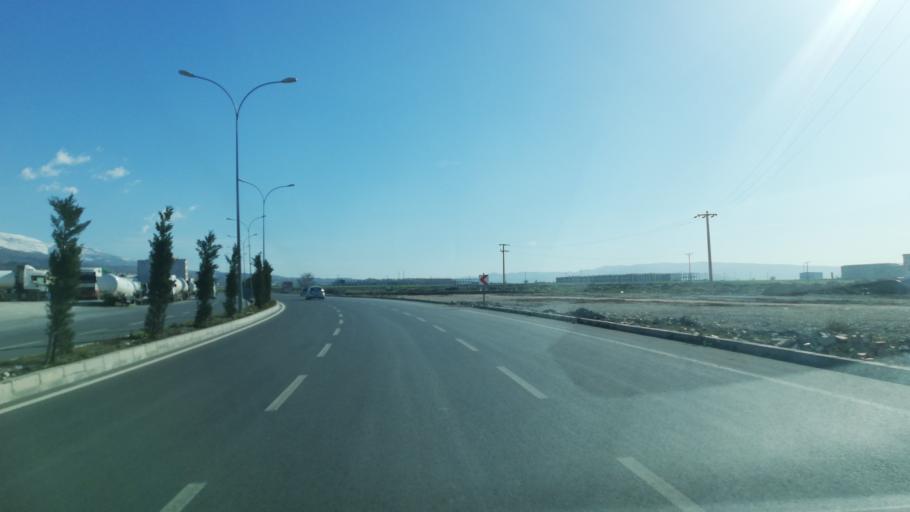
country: TR
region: Kahramanmaras
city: Kahramanmaras
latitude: 37.5706
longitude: 36.9698
